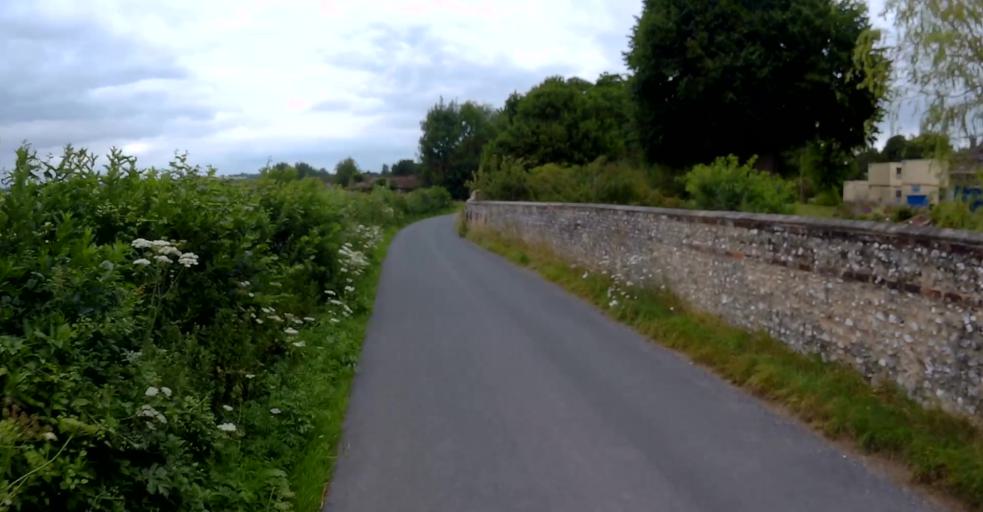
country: GB
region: England
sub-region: Hampshire
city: Kings Worthy
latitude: 51.0794
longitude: -1.2027
